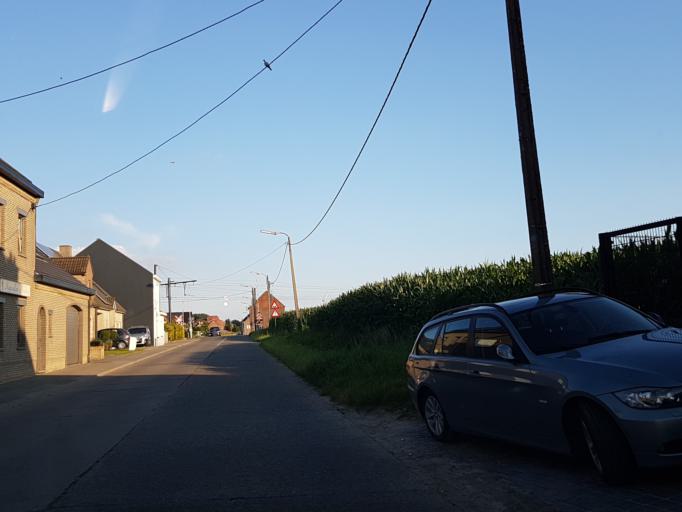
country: BE
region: Flanders
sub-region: Provincie Vlaams-Brabant
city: Merchtem
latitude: 50.9403
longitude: 4.2196
